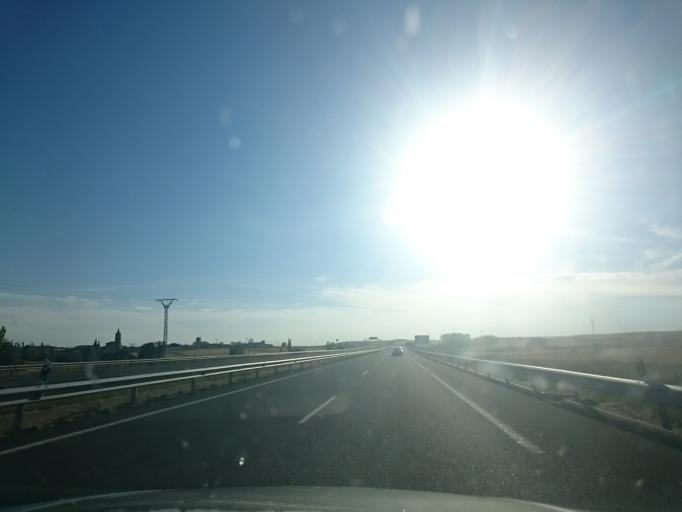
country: ES
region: Castille and Leon
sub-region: Provincia de Palencia
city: Villaherreros
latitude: 42.3926
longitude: -4.4526
